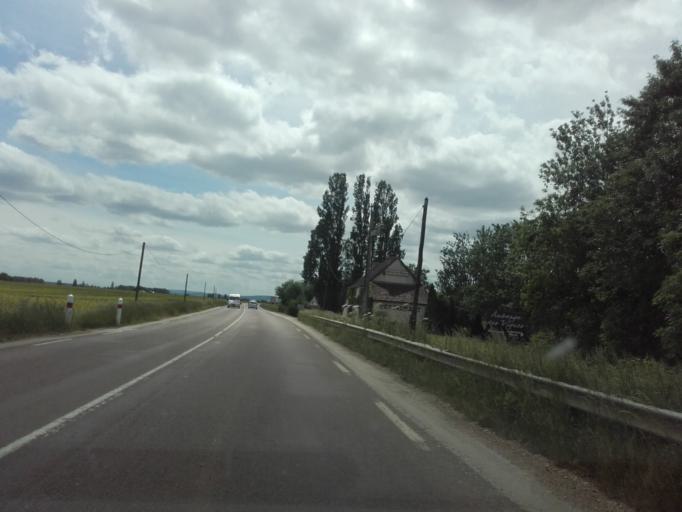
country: FR
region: Bourgogne
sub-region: Departement de la Cote-d'Or
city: Bligny-les-Beaune
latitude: 46.9998
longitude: 4.7988
